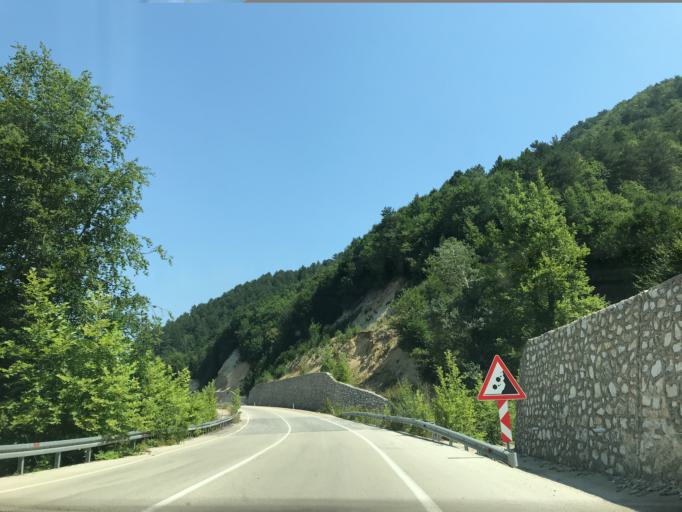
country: TR
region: Bursa
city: Tahtakopru
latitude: 39.9321
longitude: 29.5888
